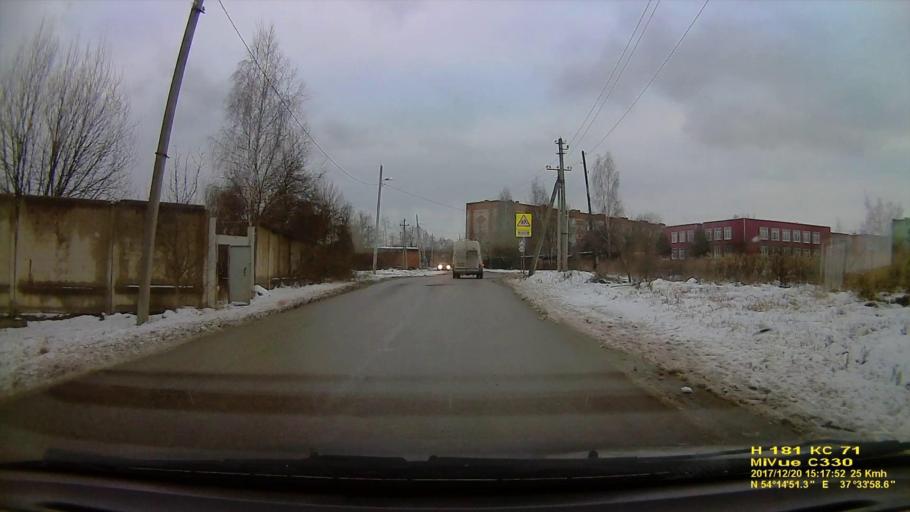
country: RU
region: Tula
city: Gorelki
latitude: 54.2475
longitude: 37.5665
